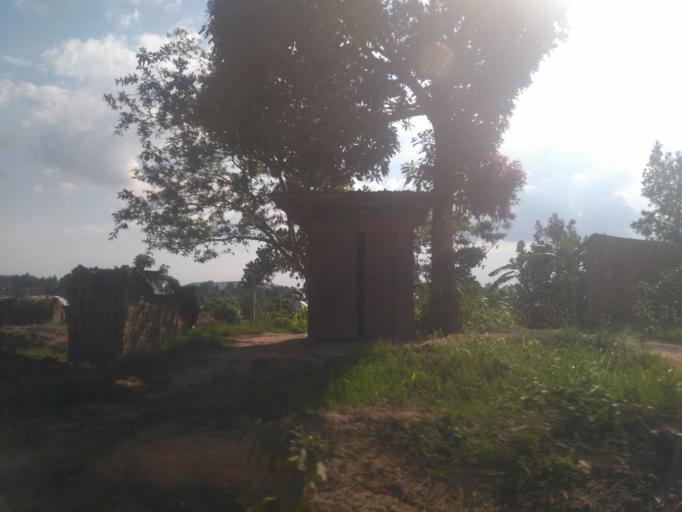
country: UG
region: Central Region
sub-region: Wakiso District
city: Wakiso
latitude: 0.2975
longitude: 32.4503
